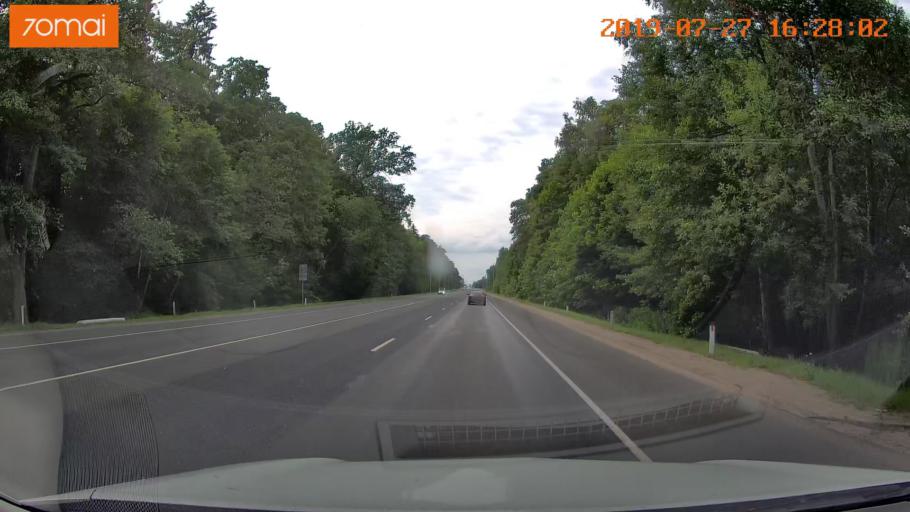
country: RU
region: Kaliningrad
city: Zheleznodorozhnyy
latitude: 54.6466
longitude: 21.3693
